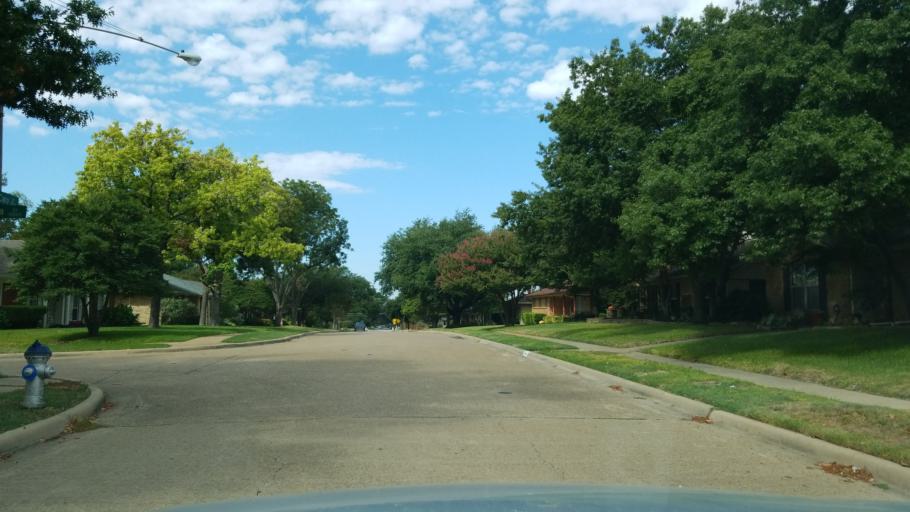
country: US
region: Texas
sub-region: Dallas County
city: Richardson
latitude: 32.9661
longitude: -96.7758
